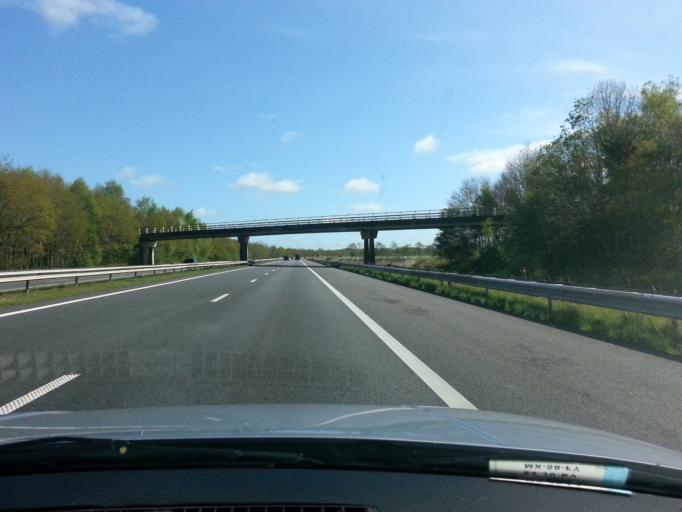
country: NL
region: Friesland
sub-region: Gemeente Smallingerland
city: Drachtstercompagnie
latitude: 53.1164
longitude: 6.1567
